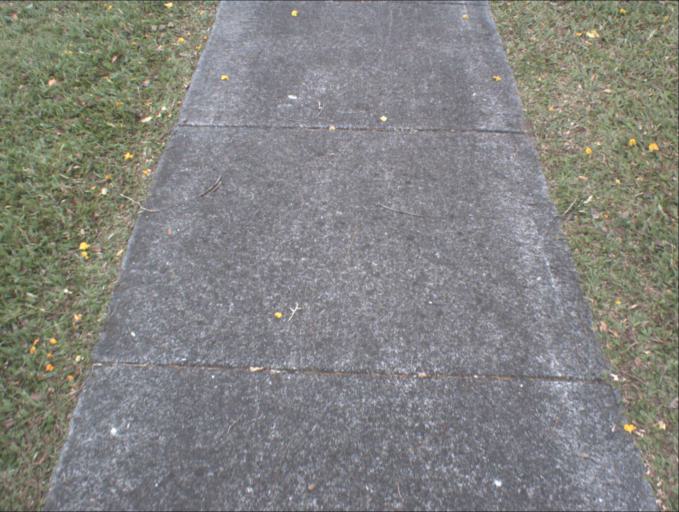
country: AU
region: Queensland
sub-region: Logan
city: Slacks Creek
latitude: -27.6320
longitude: 153.1427
